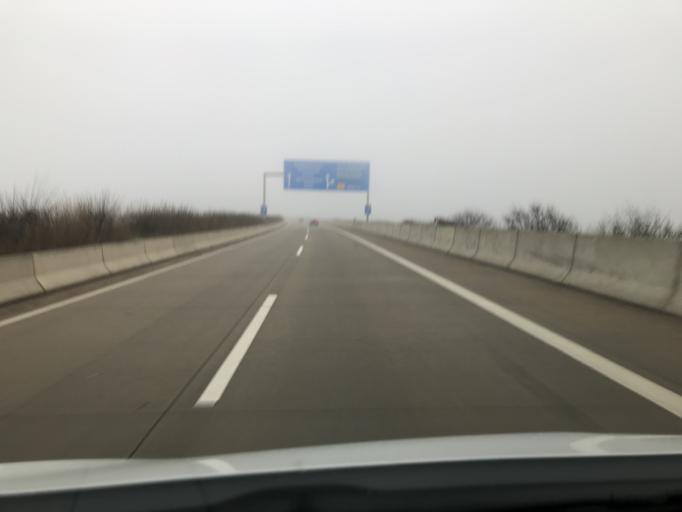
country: DE
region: Thuringia
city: Elxleben
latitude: 51.0121
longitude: 10.9587
